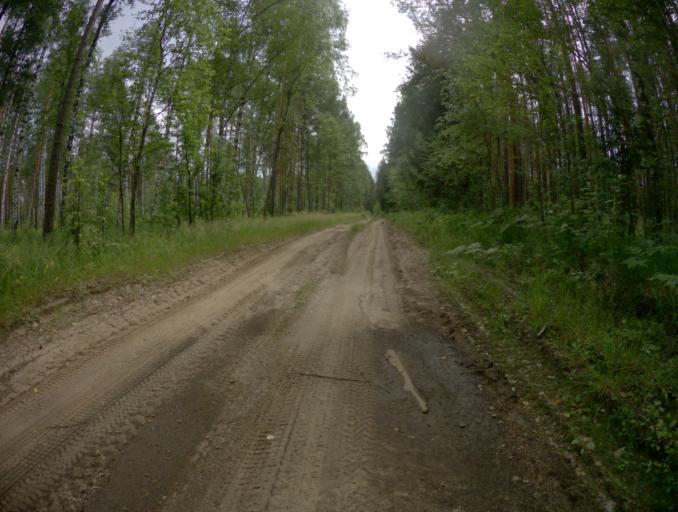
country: RU
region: Nizjnij Novgorod
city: Frolishchi
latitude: 56.3176
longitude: 42.6478
